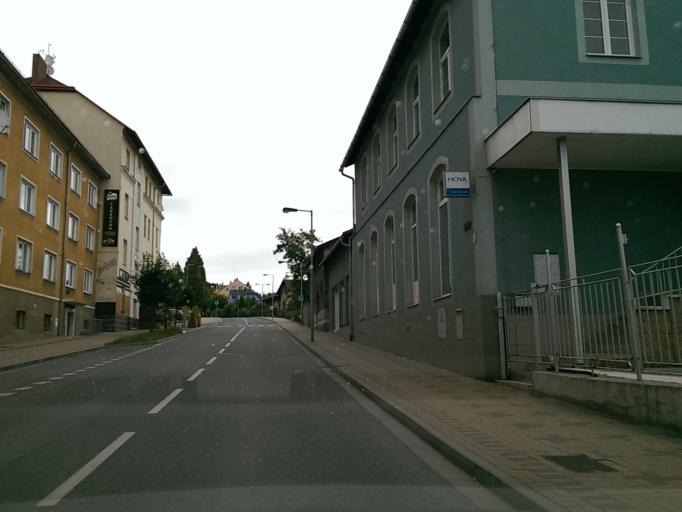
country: CZ
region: Liberecky
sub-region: Okres Semily
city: Turnov
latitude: 50.5885
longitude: 15.1476
